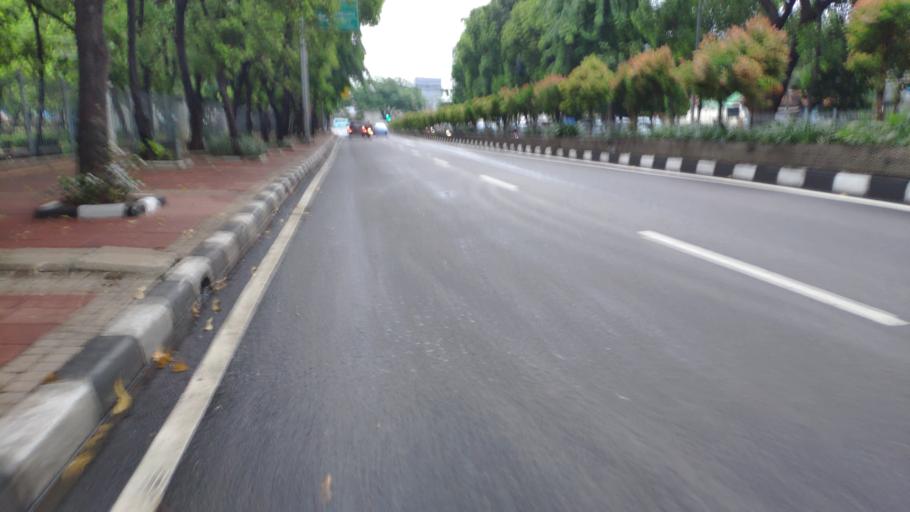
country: ID
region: Jakarta Raya
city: Jakarta
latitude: -6.2164
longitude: 106.8754
